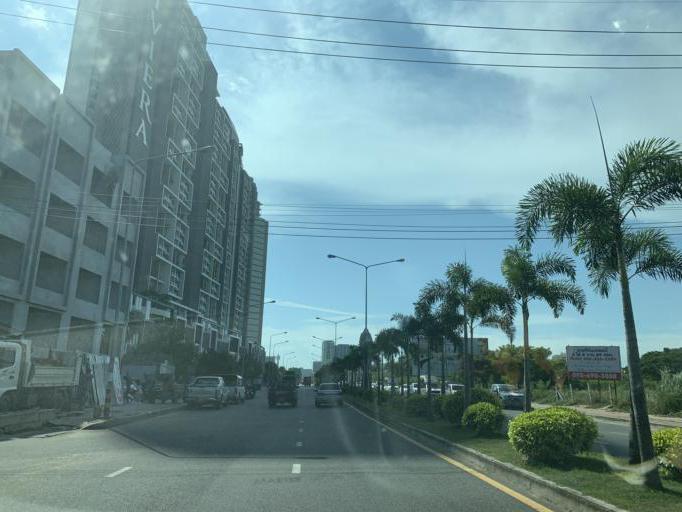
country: TH
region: Chon Buri
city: Phatthaya
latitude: 12.8818
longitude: 100.8872
